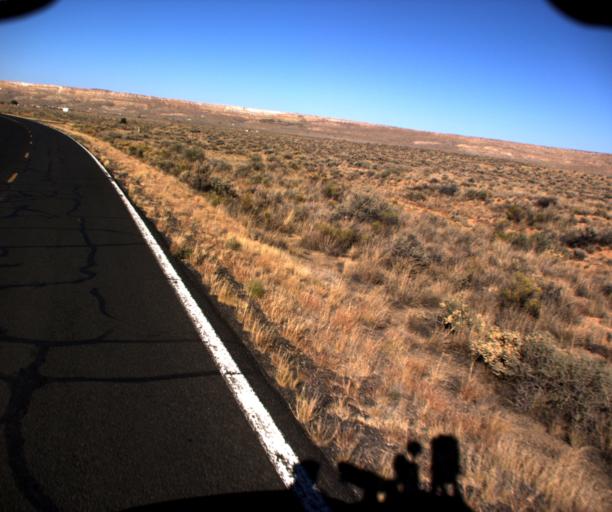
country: US
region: Arizona
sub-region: Navajo County
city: First Mesa
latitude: 35.8419
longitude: -110.3250
